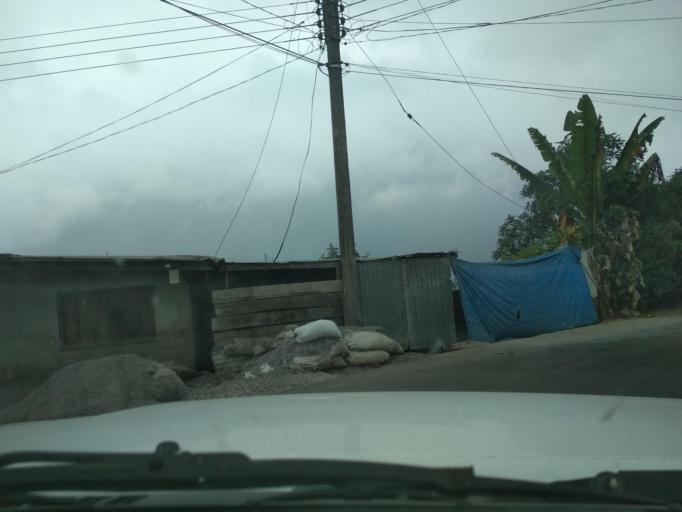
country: MX
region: Veracruz
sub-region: La Perla
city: Metlac Hernandez (Metlac Primero)
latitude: 18.9601
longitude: -97.1583
